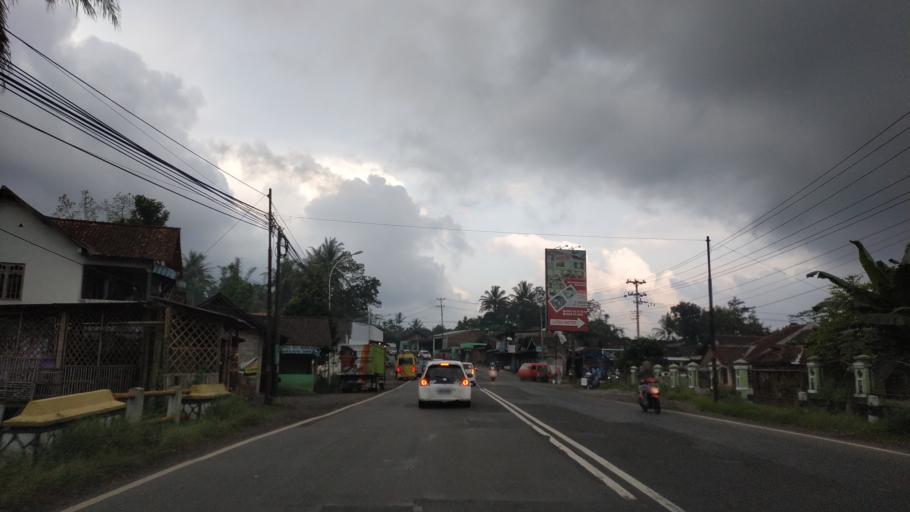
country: ID
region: Central Java
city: Salatiga
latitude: -7.2931
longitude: 110.4686
